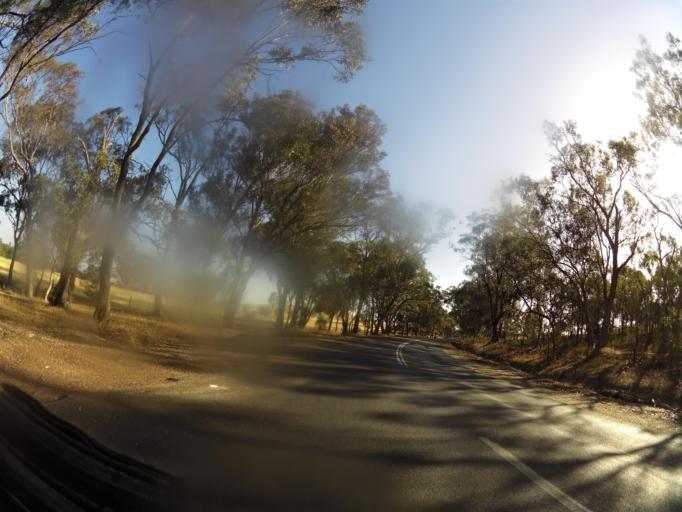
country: AU
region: Victoria
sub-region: Murrindindi
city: Kinglake West
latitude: -37.0084
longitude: 145.1241
